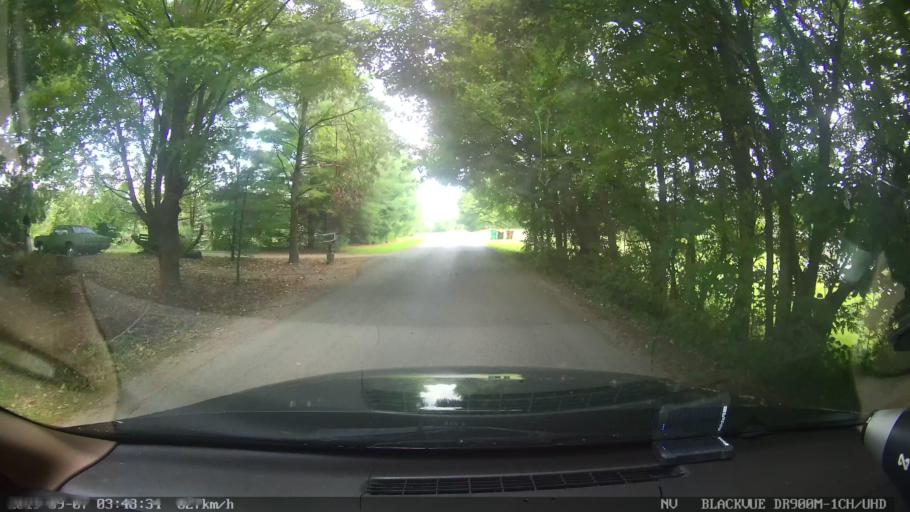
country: US
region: Ohio
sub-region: Licking County
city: Granville
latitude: 40.1476
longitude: -82.5430
